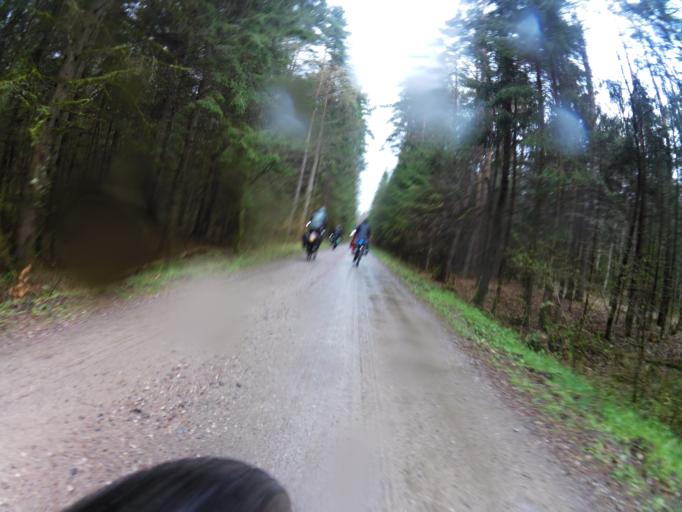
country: PL
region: Pomeranian Voivodeship
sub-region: Powiat slupski
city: Kepice
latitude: 54.2644
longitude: 16.7962
